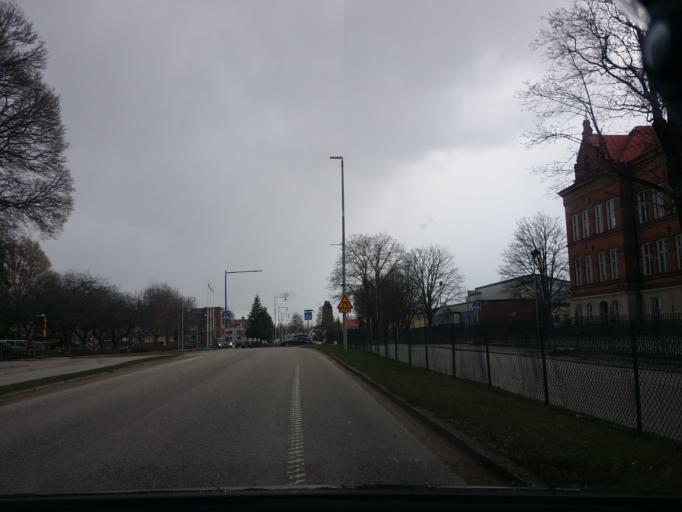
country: SE
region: Vaestmanland
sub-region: Sala Kommun
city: Sala
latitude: 59.9191
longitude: 16.6013
